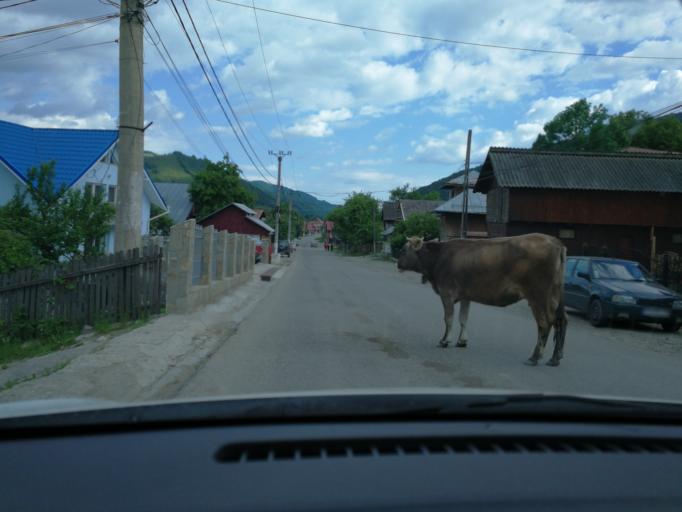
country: RO
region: Prahova
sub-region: Comuna Valea Doftanei
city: Tesila
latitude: 45.2950
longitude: 25.7209
